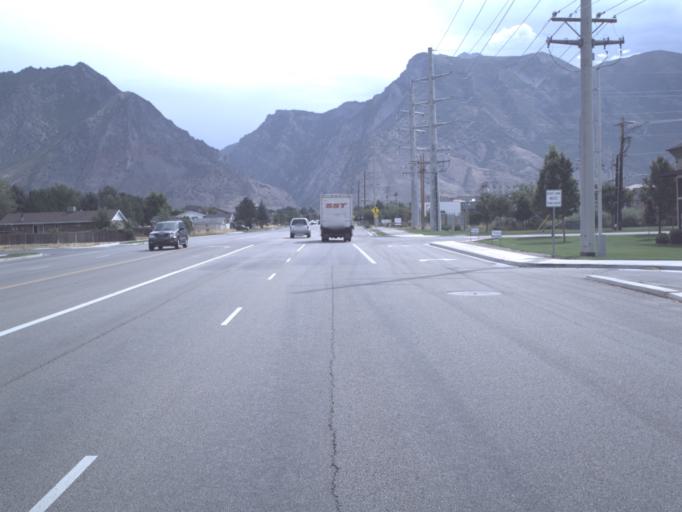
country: US
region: Utah
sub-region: Utah County
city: Alpine
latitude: 40.4318
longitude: -111.7935
